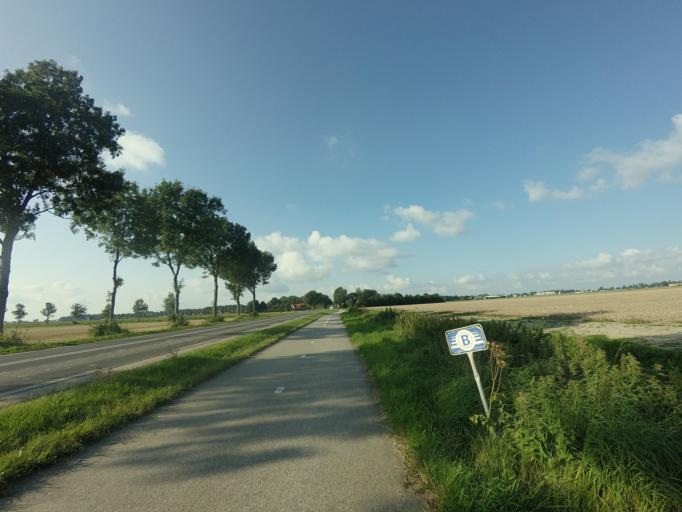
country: NL
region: Flevoland
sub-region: Gemeente Noordoostpolder
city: Ens
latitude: 52.6984
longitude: 5.8617
